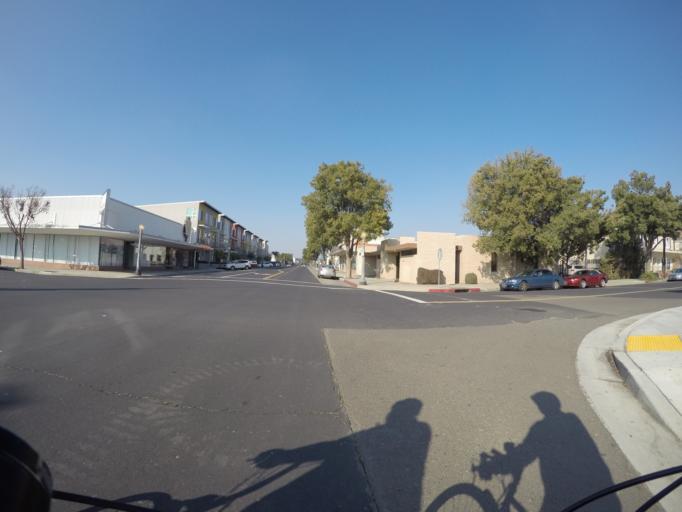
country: US
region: California
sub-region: Fresno County
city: Fresno
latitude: 36.7408
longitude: -119.7976
